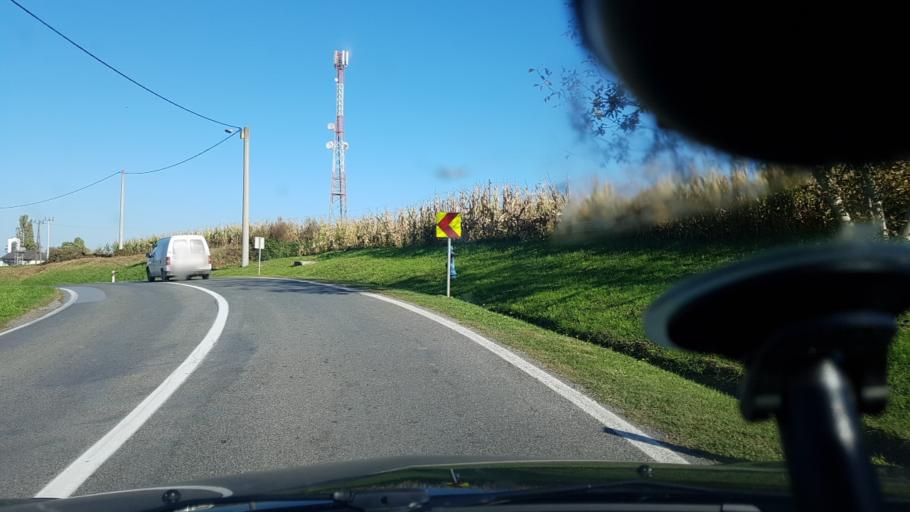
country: HR
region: Bjelovarsko-Bilogorska
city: Gudovac
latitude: 45.7997
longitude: 16.7163
